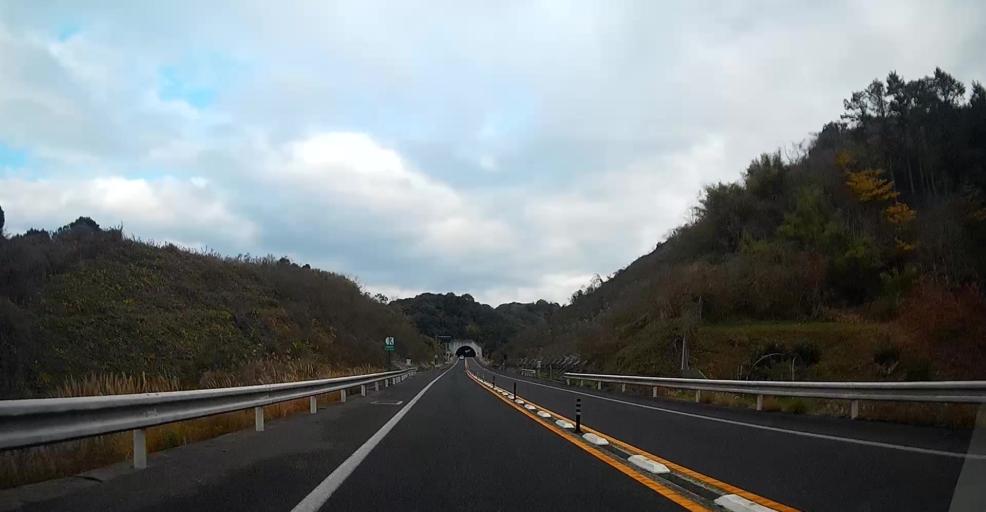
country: JP
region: Kumamoto
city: Hondo
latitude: 32.5041
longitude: 130.3100
